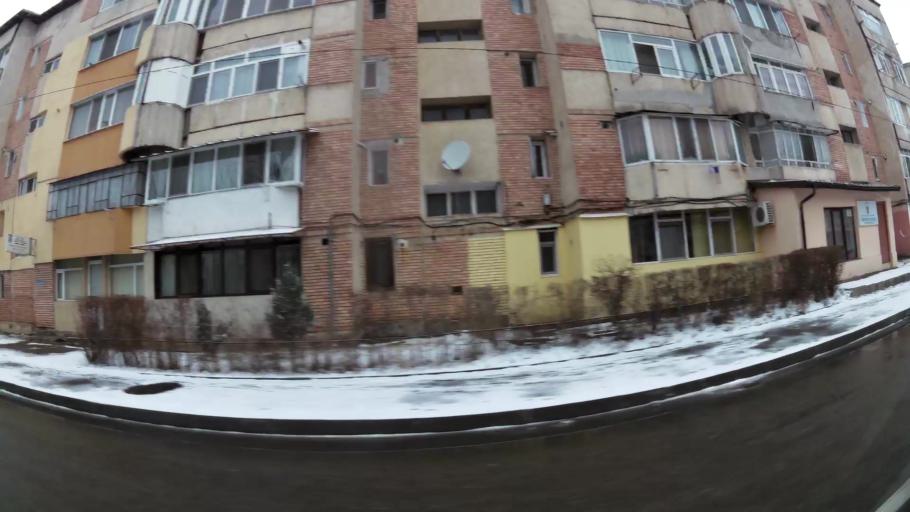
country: RO
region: Dambovita
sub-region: Municipiul Targoviste
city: Targoviste
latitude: 44.9194
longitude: 25.4738
